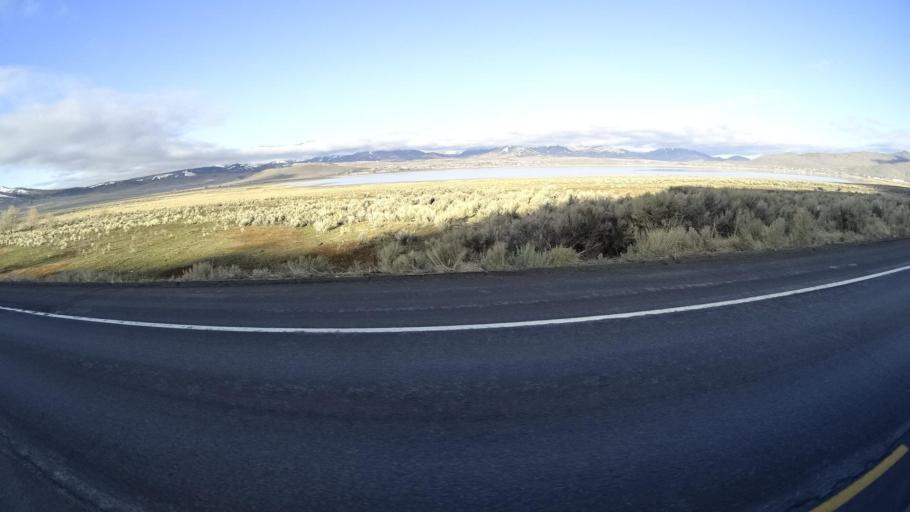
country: US
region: Nevada
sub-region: Washoe County
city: Cold Springs
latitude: 39.6562
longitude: -119.9585
